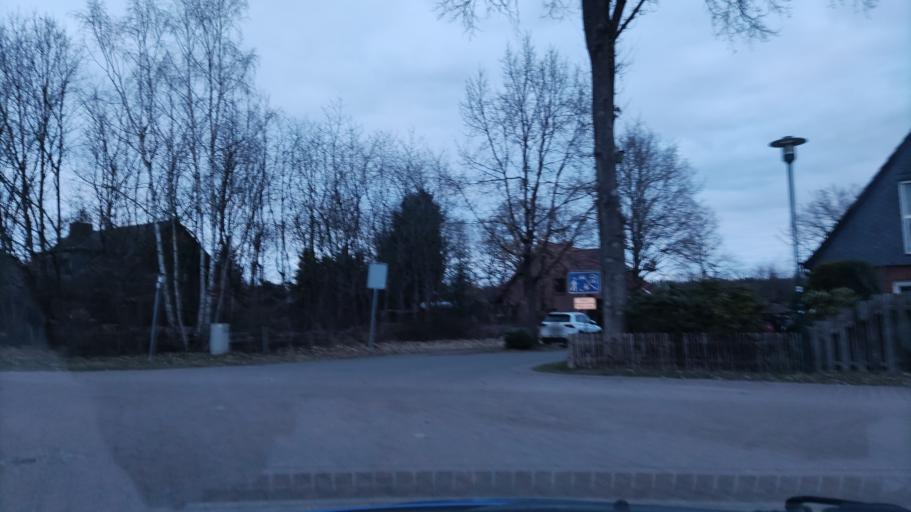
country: DE
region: Lower Saxony
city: Wendisch Evern
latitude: 53.2146
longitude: 10.4799
